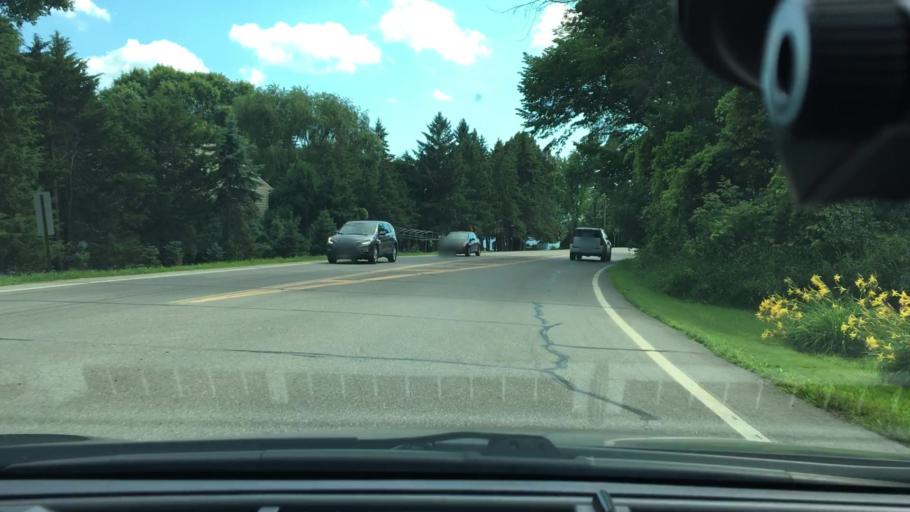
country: US
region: Minnesota
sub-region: Hennepin County
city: Tonka Bay
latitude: 44.9392
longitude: -93.5825
